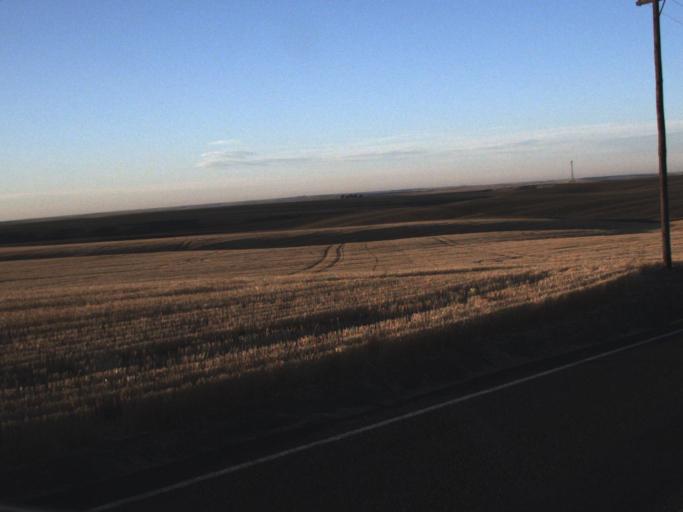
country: US
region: Washington
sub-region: Adams County
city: Ritzville
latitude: 46.9099
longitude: -118.5676
